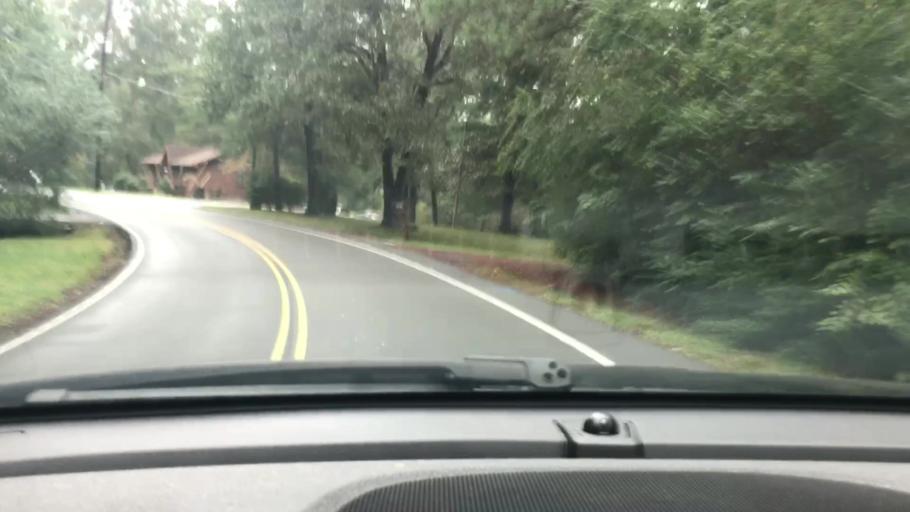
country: US
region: Tennessee
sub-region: Cheatham County
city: Kingston Springs
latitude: 36.1070
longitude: -87.1370
